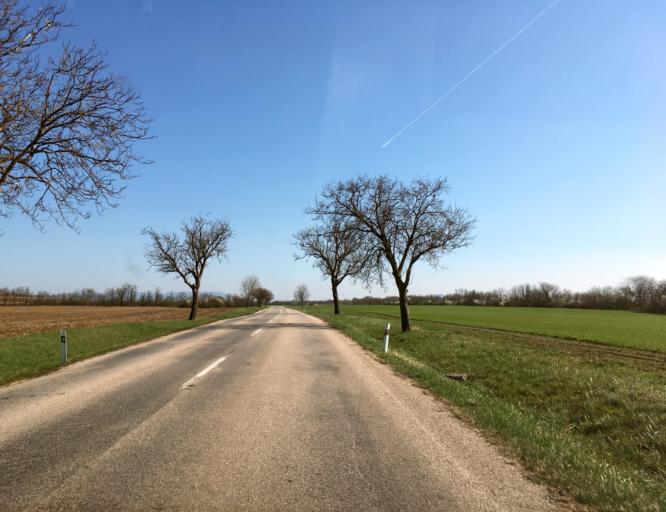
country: HU
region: Komarom-Esztergom
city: Nyergesujfalu
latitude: 47.8271
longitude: 18.5573
